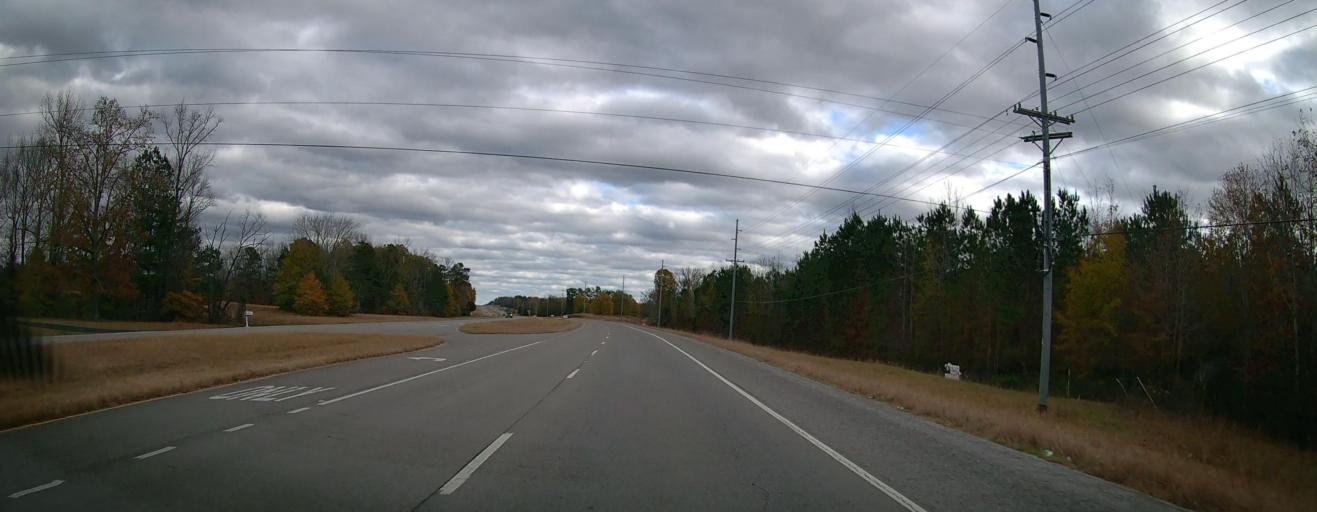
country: US
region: Alabama
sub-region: Lawrence County
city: Town Creek
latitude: 34.5753
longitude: -87.4014
